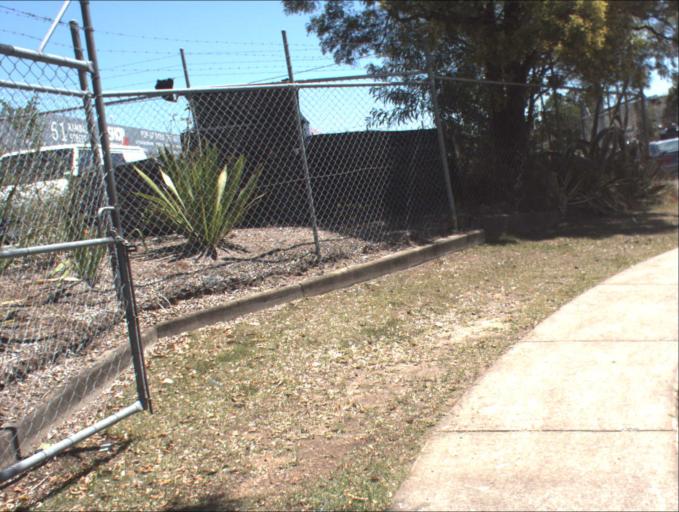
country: AU
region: Queensland
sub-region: Logan
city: Springwood
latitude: -27.6244
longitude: 153.1241
